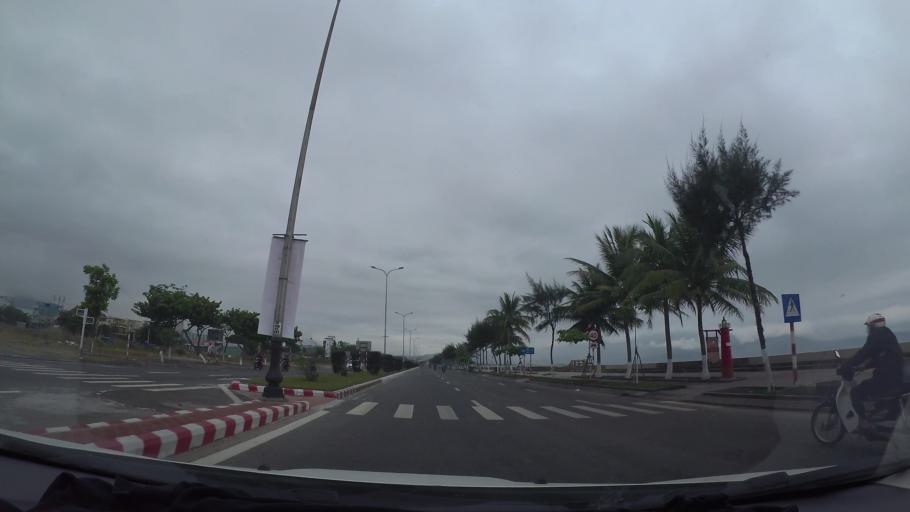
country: VN
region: Da Nang
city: Lien Chieu
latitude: 16.0816
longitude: 108.1660
